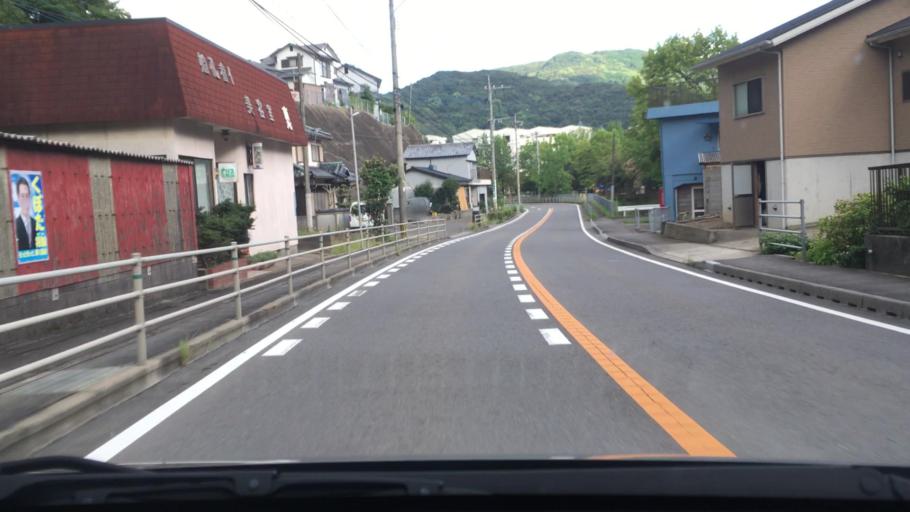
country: JP
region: Nagasaki
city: Togitsu
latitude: 32.8266
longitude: 129.7728
